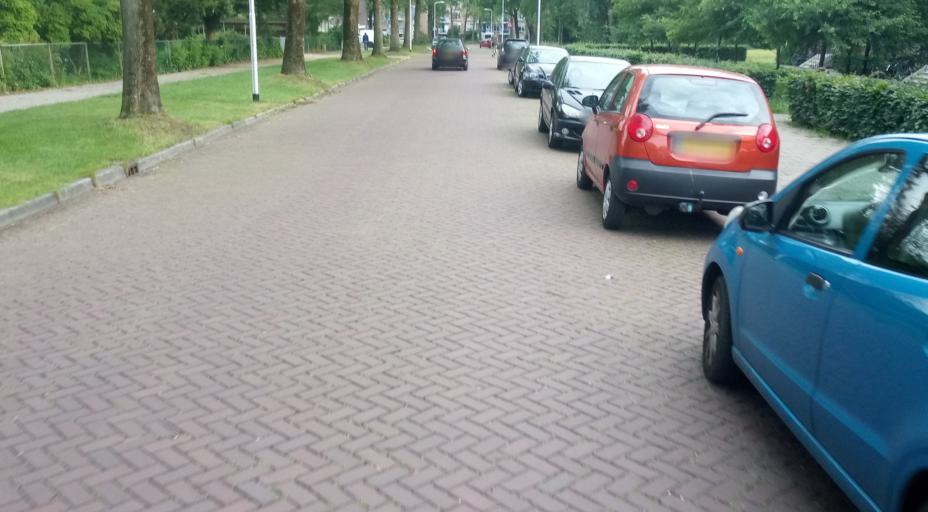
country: NL
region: Gelderland
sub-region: Gemeente Zutphen
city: Zutphen
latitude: 52.1392
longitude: 6.2143
